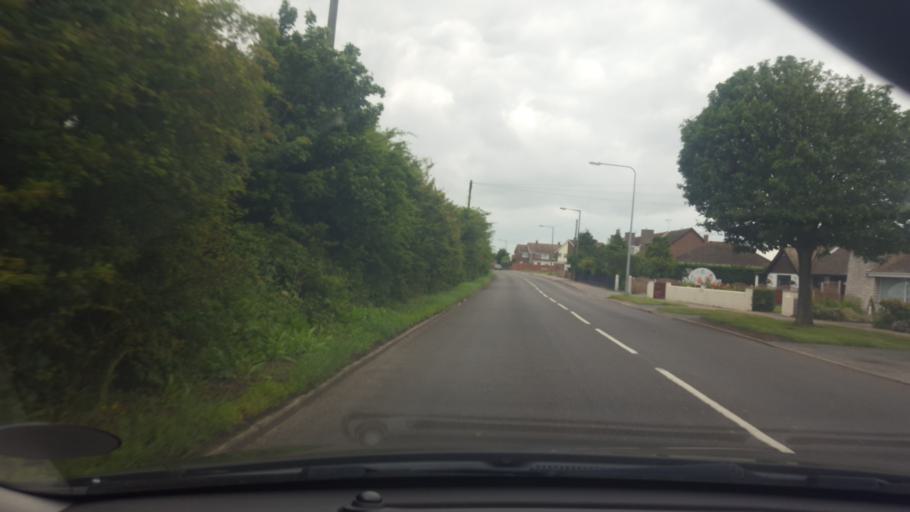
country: GB
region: England
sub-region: Essex
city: Clacton-on-Sea
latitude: 51.7881
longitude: 1.1199
